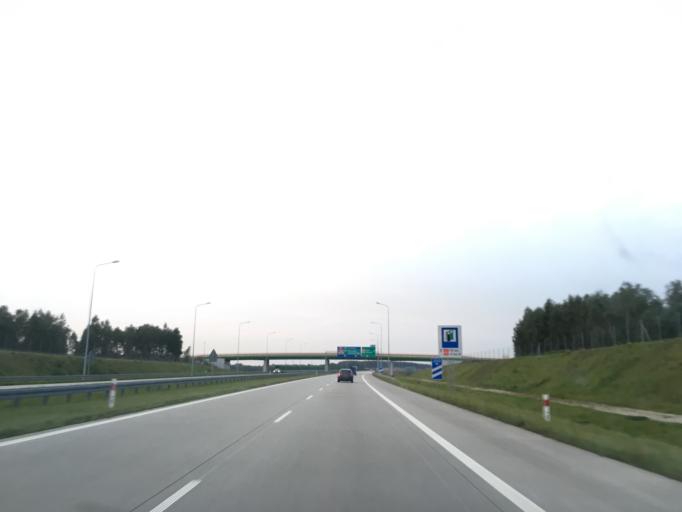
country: PL
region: Lodz Voivodeship
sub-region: Powiat piotrkowski
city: Czarnocin
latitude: 51.5576
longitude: 19.6039
